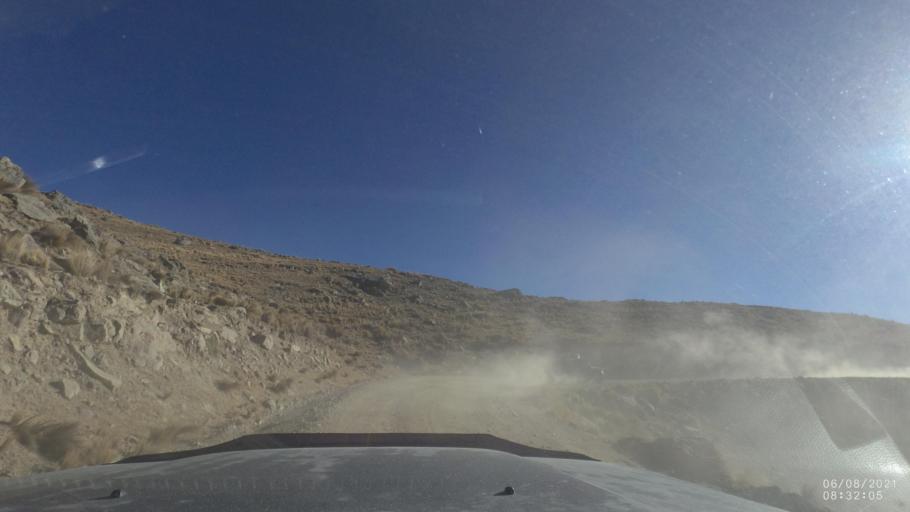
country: BO
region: Cochabamba
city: Sipe Sipe
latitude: -17.1827
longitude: -66.3735
